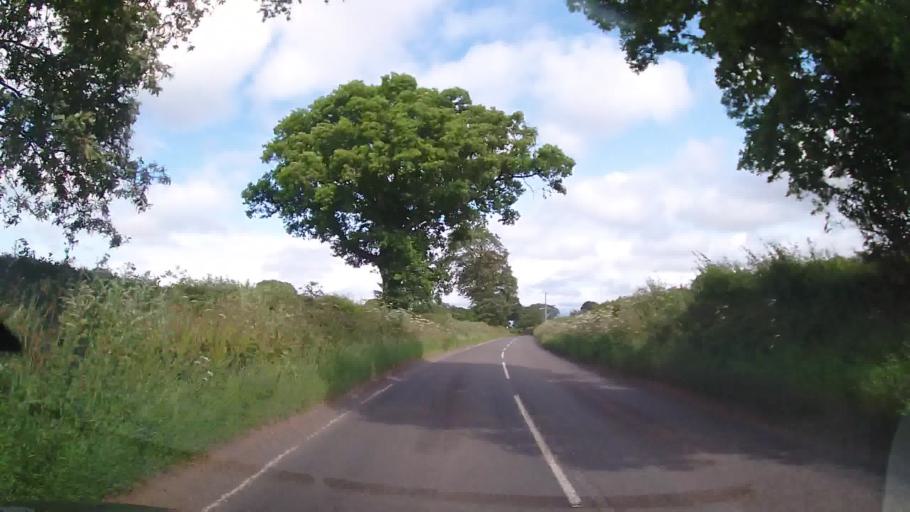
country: GB
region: England
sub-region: Shropshire
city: Great Ness
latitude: 52.7984
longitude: -2.9331
